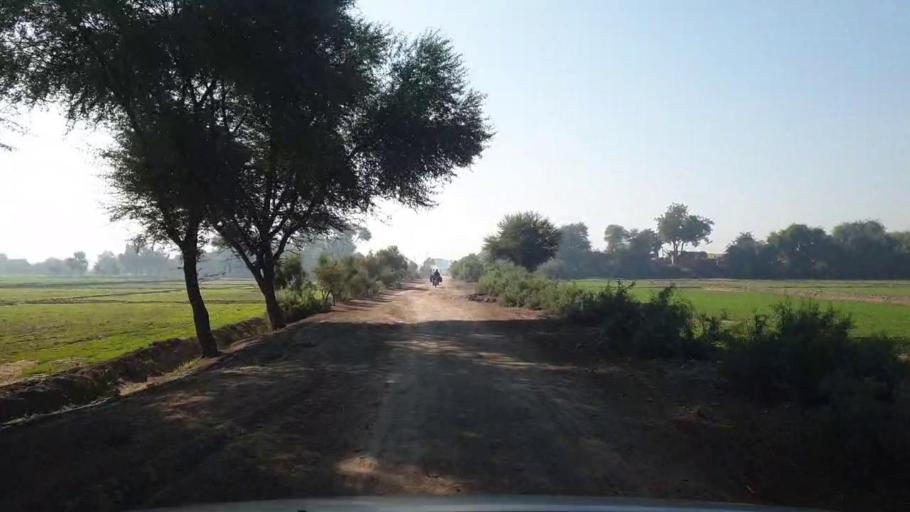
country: PK
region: Sindh
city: Dadu
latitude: 26.6413
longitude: 67.8209
